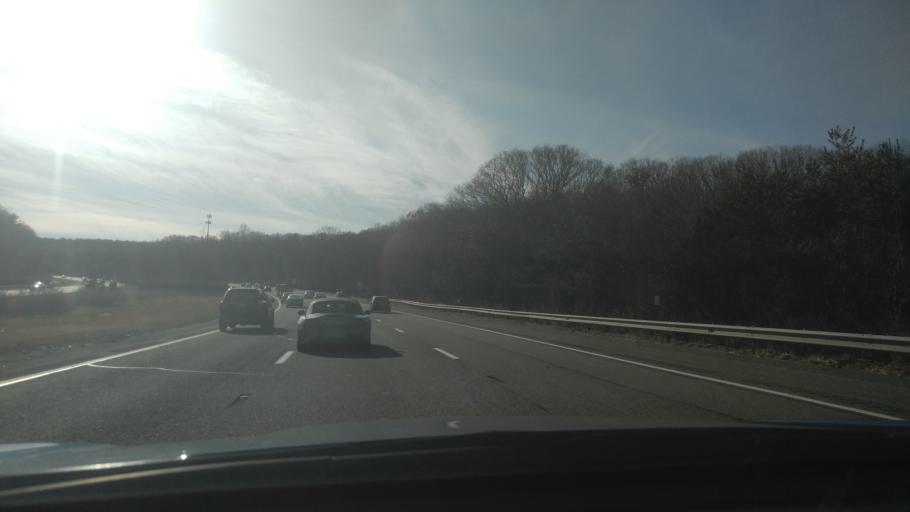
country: US
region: Rhode Island
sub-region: Providence County
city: Smithfield
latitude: 41.9018
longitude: -71.5203
